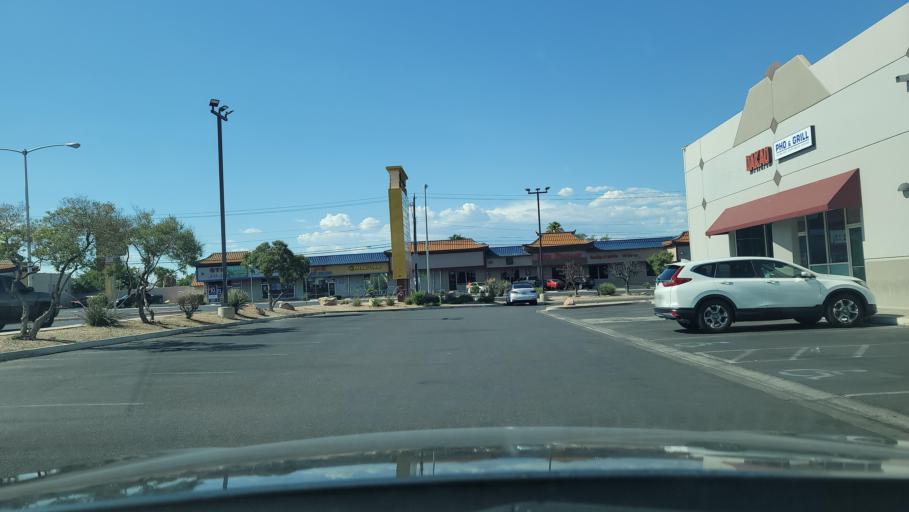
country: US
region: Nevada
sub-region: Clark County
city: Spring Valley
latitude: 36.1257
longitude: -115.2028
